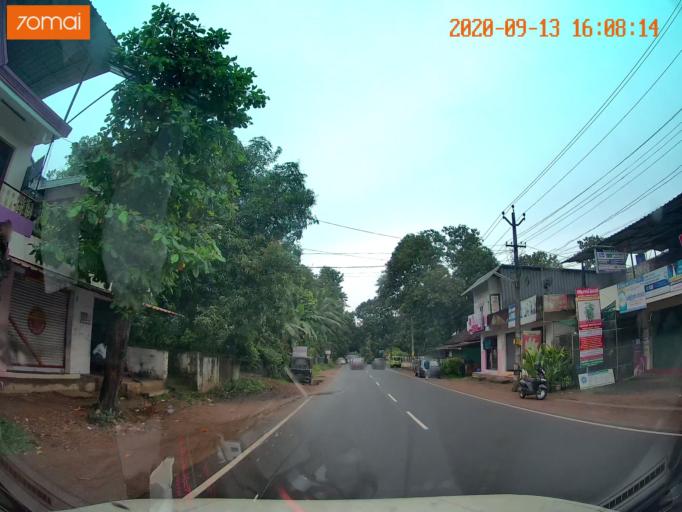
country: IN
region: Kerala
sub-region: Kottayam
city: Palackattumala
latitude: 9.6762
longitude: 76.5914
